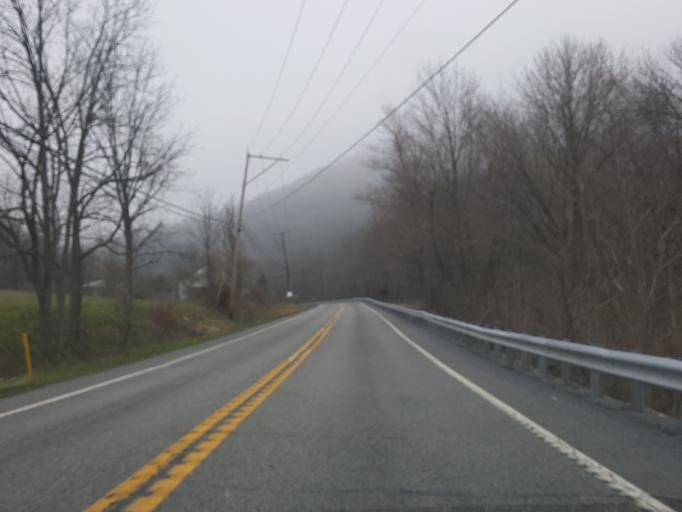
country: US
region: Pennsylvania
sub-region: Lebanon County
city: Jonestown
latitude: 40.4733
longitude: -76.5197
